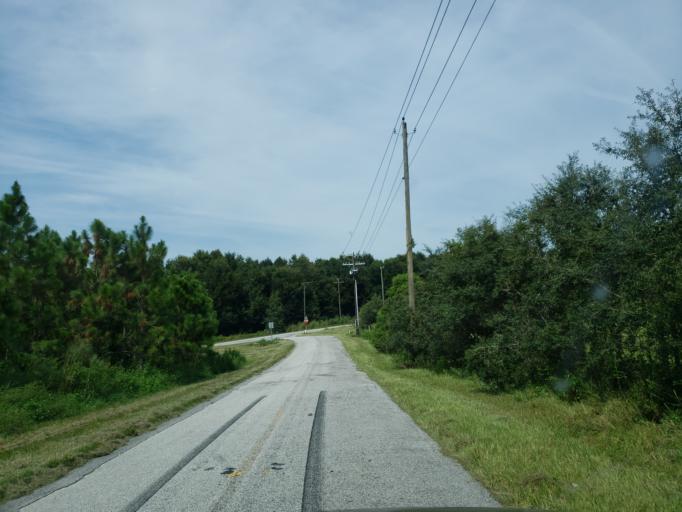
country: US
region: Florida
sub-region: Pasco County
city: Saint Leo
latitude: 28.4152
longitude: -82.2680
